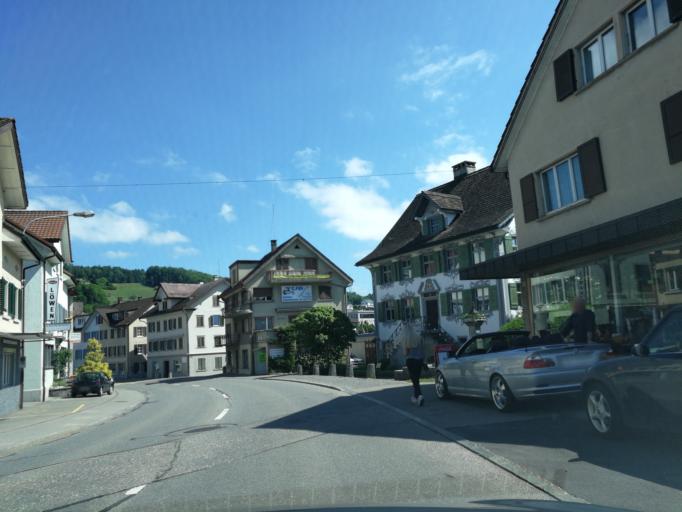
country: CH
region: Saint Gallen
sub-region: Wahlkreis See-Gaster
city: Eschenbach
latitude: 47.2394
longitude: 8.9216
